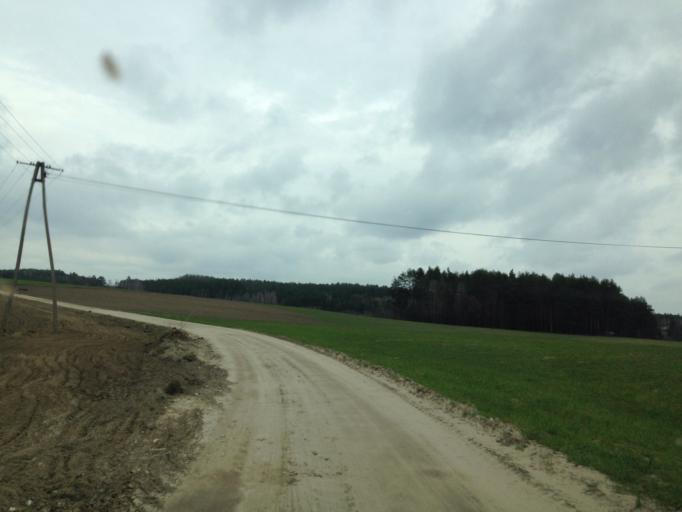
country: PL
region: Warmian-Masurian Voivodeship
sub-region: Powiat dzialdowski
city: Lidzbark
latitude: 53.2124
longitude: 19.7452
